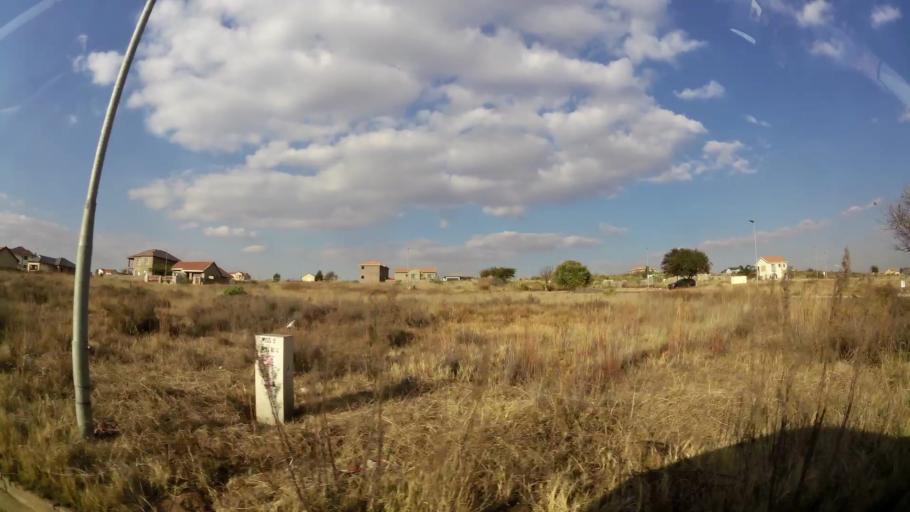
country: ZA
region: Gauteng
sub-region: West Rand District Municipality
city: Krugersdorp
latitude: -26.1013
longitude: 27.7294
